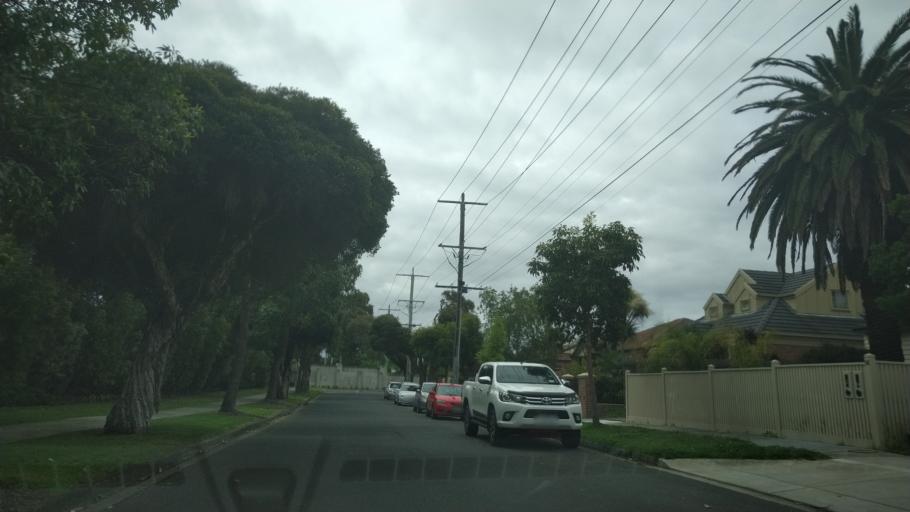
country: AU
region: Victoria
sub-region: Monash
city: Chadstone
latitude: -37.8879
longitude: 145.0861
